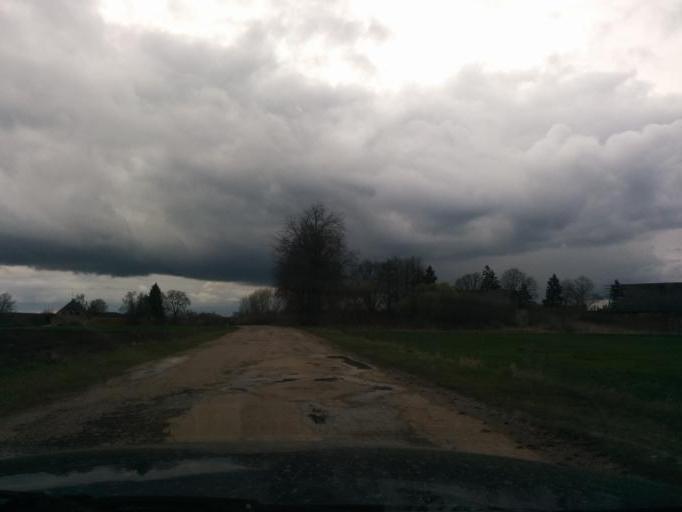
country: LV
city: Tervete
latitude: 56.3648
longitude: 23.5060
